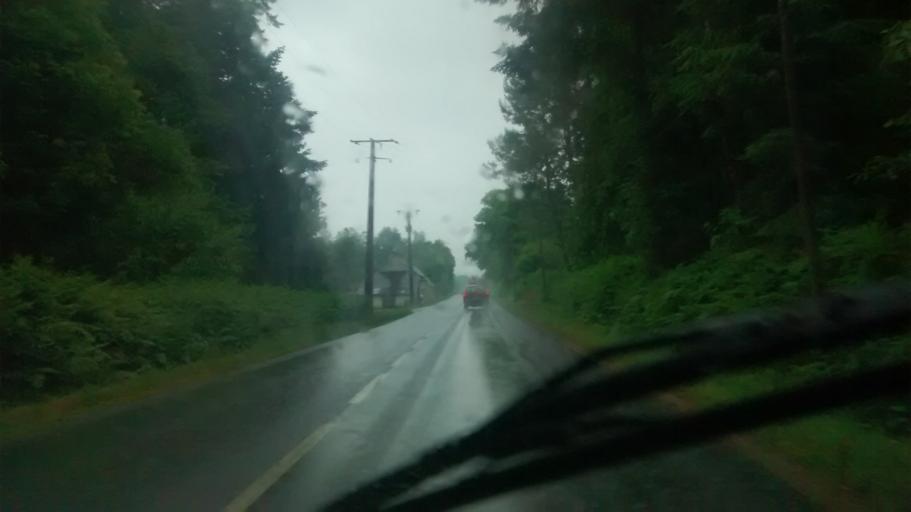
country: FR
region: Brittany
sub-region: Departement du Morbihan
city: La Gacilly
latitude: 47.7812
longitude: -2.1728
